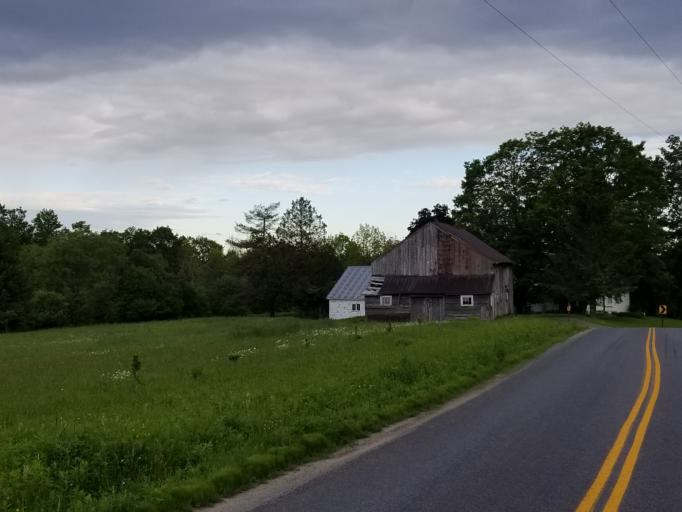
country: US
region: New York
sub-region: Herkimer County
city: Herkimer
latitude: 43.1942
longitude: -74.9522
